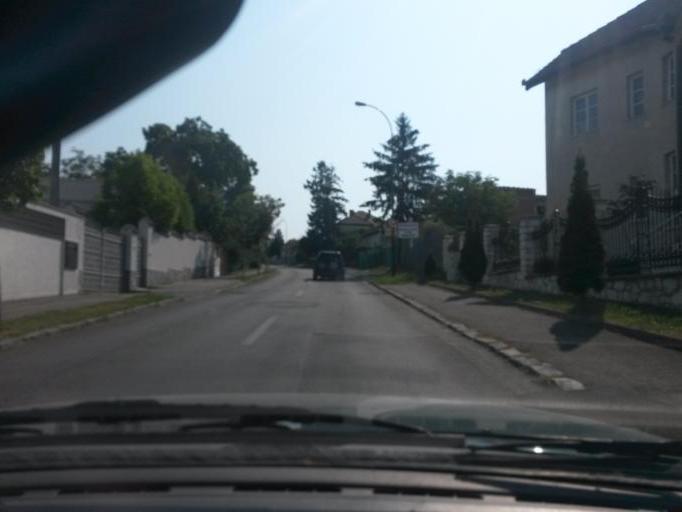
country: RO
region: Mures
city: Targu-Mures
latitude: 46.5416
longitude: 24.5734
